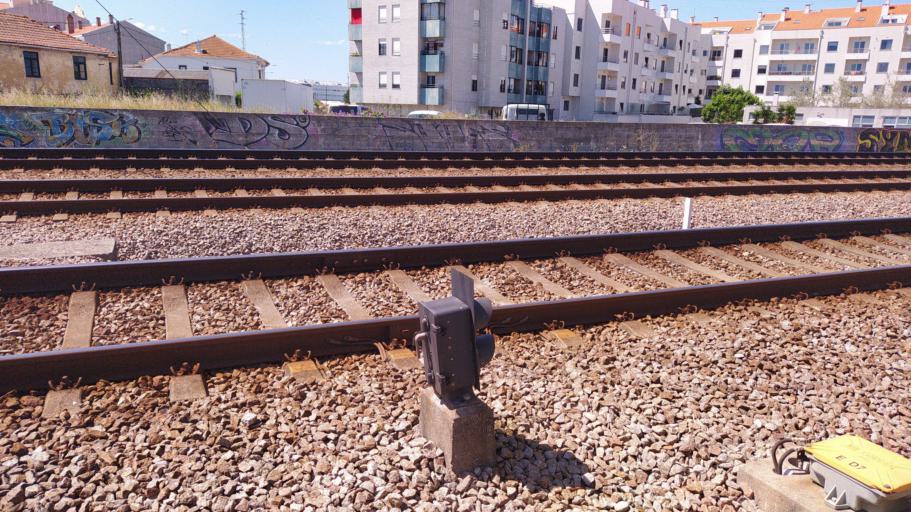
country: PT
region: Aveiro
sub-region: Aveiro
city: Aveiro
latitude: 40.6470
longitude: -8.6384
